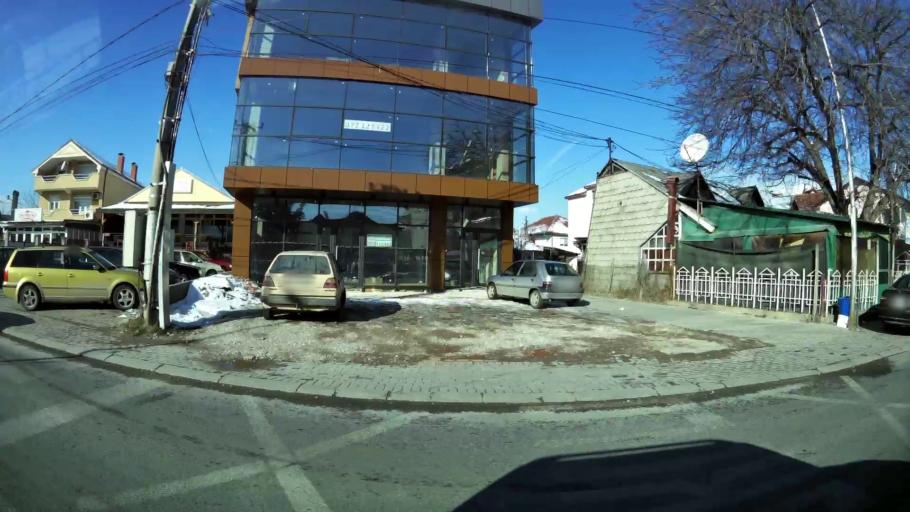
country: MK
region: Saraj
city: Saraj
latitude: 41.9987
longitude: 21.3268
